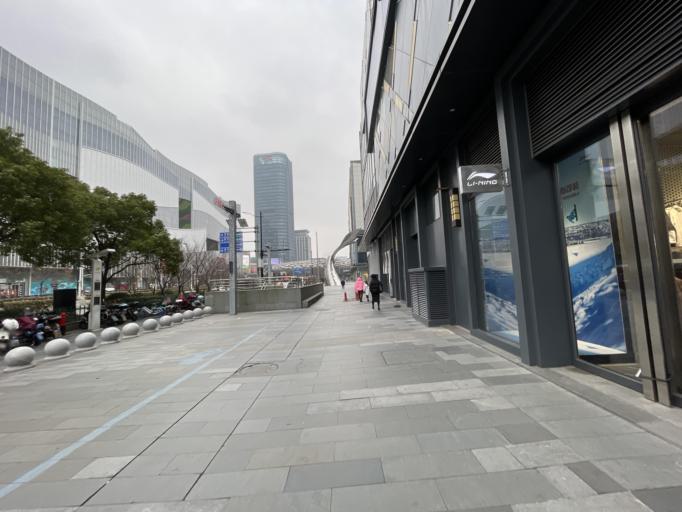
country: CN
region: Shanghai Shi
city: Yangpu
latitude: 31.3041
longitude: 121.5098
